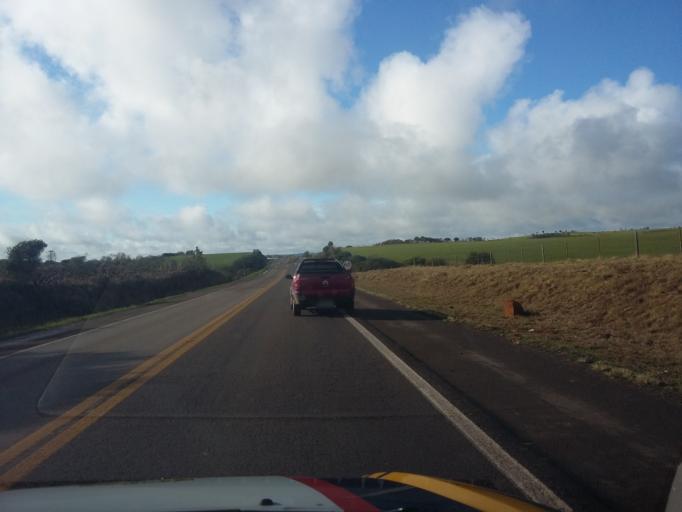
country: BR
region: Rio Grande do Sul
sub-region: Vacaria
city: Vacaria
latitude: -28.5323
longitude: -50.8025
